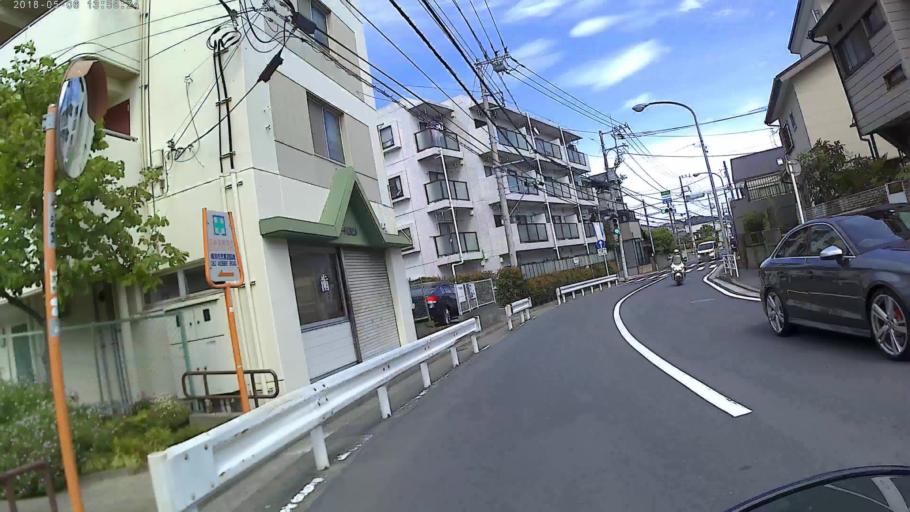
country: JP
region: Kanagawa
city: Yokohama
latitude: 35.4395
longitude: 139.5901
